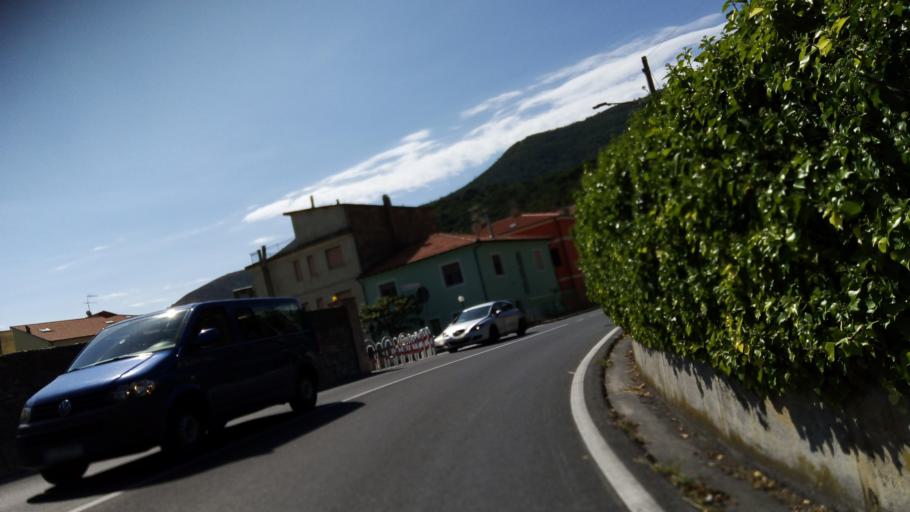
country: IT
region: Liguria
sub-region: Provincia di Savona
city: Toirano
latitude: 44.1285
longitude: 8.2052
